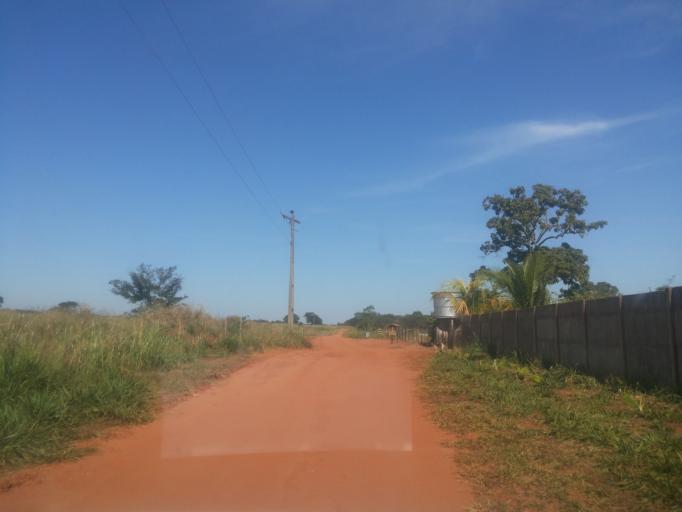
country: BR
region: Minas Gerais
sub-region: Santa Vitoria
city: Santa Vitoria
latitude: -18.9894
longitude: -50.3718
